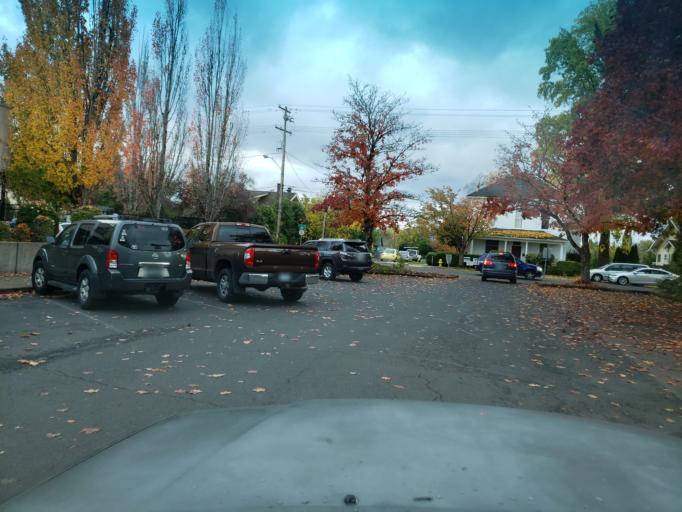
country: US
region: Oregon
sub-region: Yamhill County
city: McMinnville
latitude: 45.2090
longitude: -123.1924
